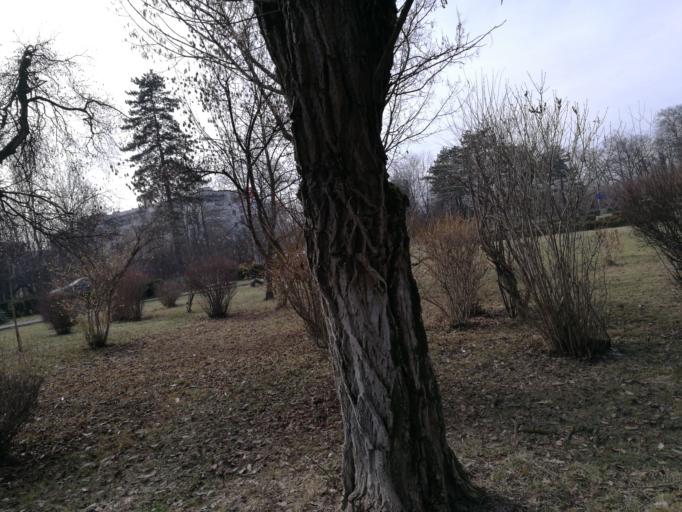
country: RO
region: Ilfov
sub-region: Comuna Otopeni
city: Otopeni
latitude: 44.5168
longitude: 26.0912
